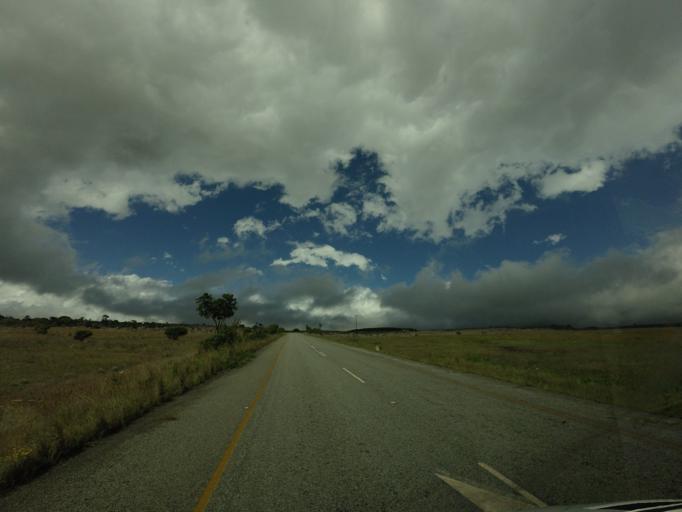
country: ZA
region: Mpumalanga
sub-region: Ehlanzeni District
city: Graksop
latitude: -24.8630
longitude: 30.8602
